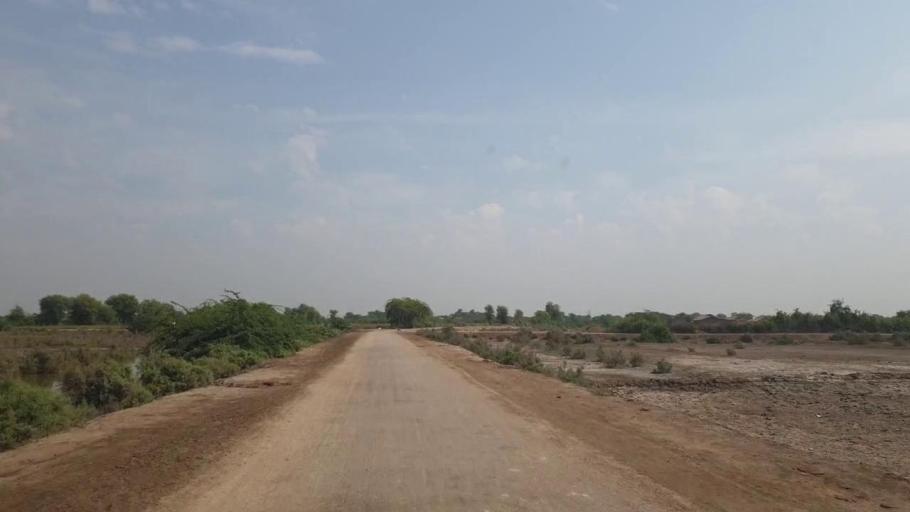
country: PK
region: Sindh
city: Rajo Khanani
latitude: 24.9562
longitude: 69.0166
